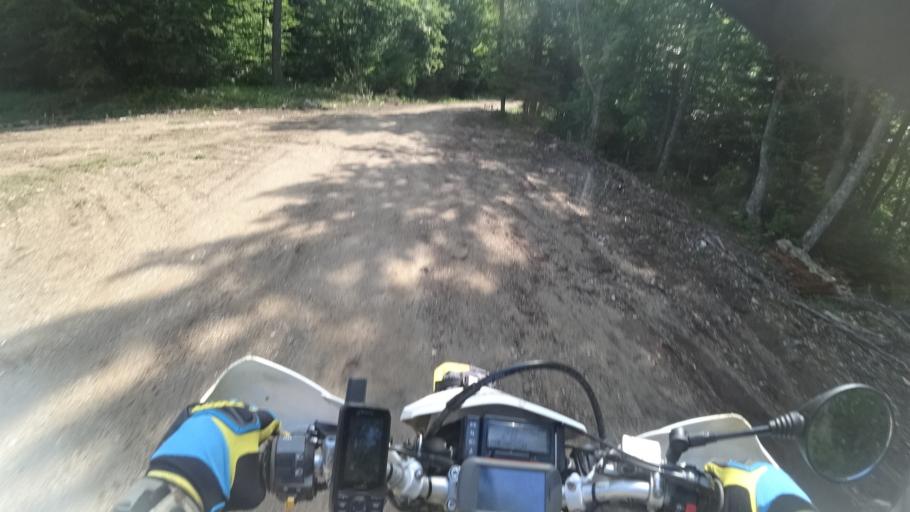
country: BA
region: Federation of Bosnia and Herzegovina
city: Izacic
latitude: 44.7605
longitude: 15.7541
